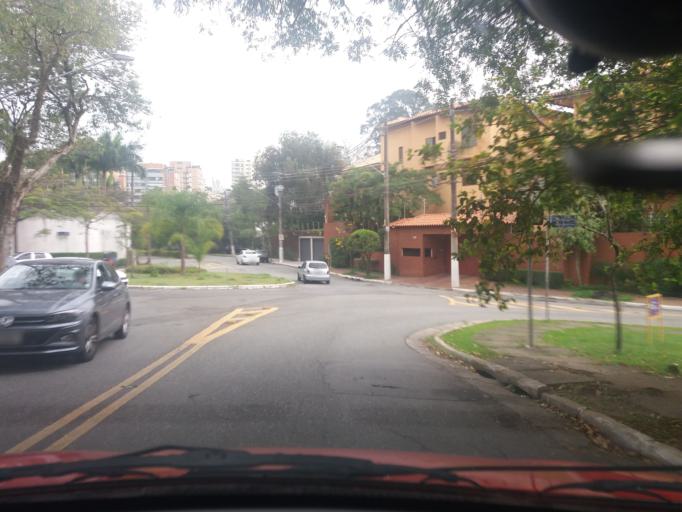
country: BR
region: Sao Paulo
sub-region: Taboao Da Serra
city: Taboao da Serra
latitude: -23.5943
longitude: -46.7157
